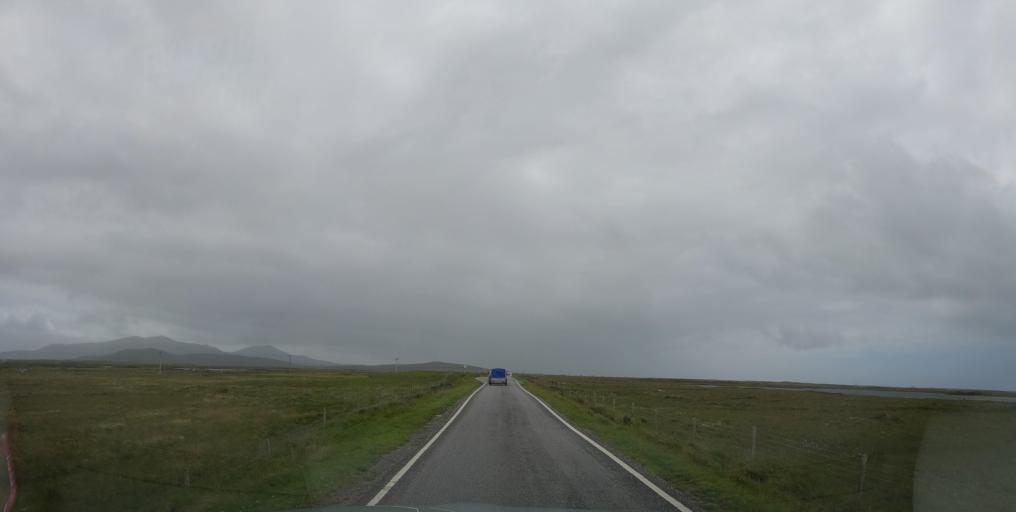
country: GB
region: Scotland
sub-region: Eilean Siar
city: Benbecula
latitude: 57.3753
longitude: -7.3452
